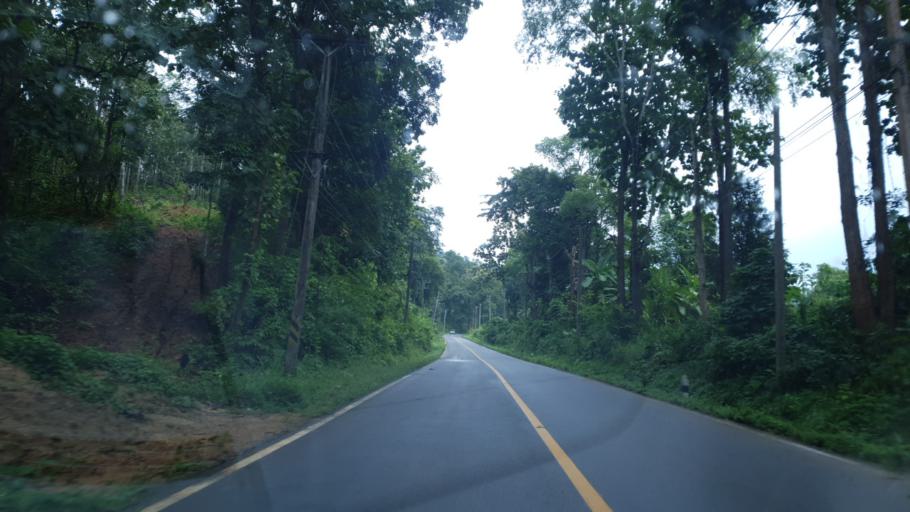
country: TH
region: Mae Hong Son
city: Ban Huai I Huak
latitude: 18.1382
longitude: 97.9885
